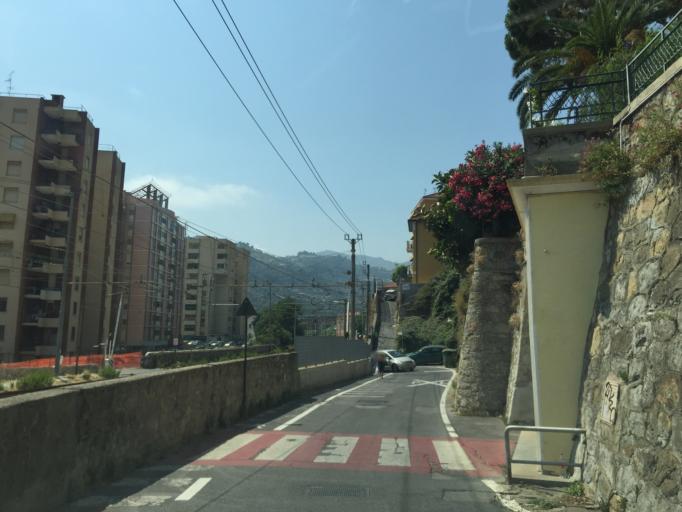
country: IT
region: Liguria
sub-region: Provincia di Imperia
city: Ventimiglia
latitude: 43.7942
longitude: 7.6070
